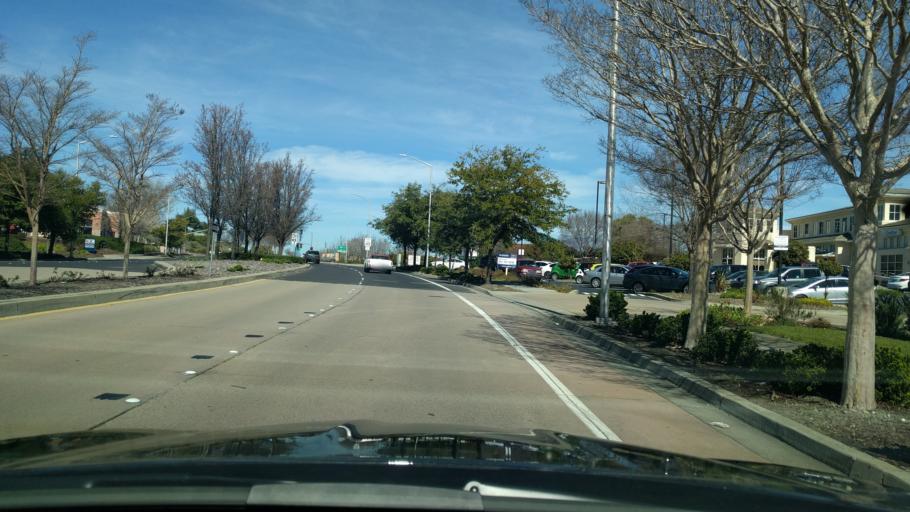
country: US
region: California
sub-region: Alameda County
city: Dublin
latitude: 37.7234
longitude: -121.9422
